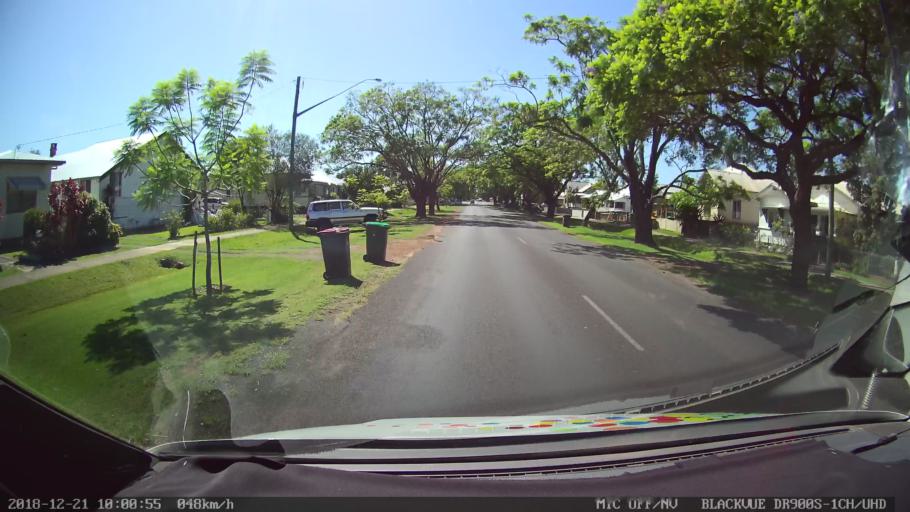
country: AU
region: New South Wales
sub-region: Clarence Valley
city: Grafton
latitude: -29.6855
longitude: 152.9284
